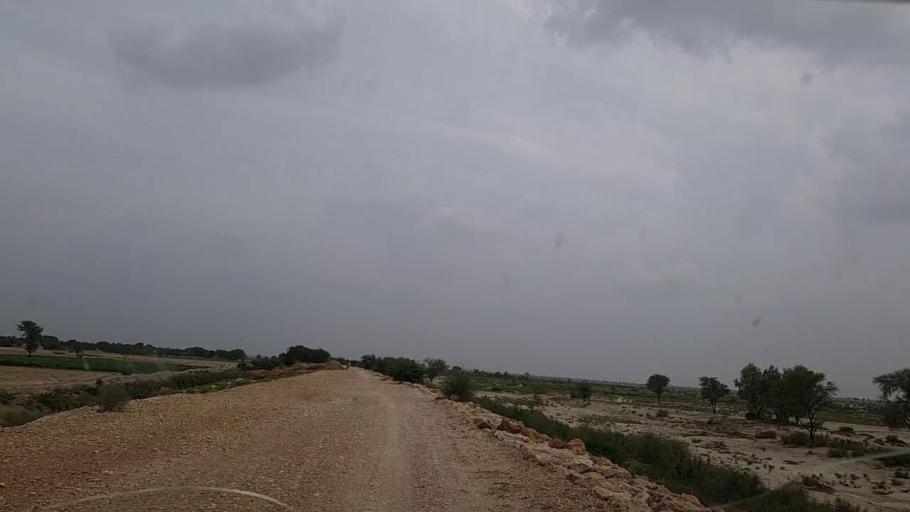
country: PK
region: Sindh
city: Johi
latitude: 26.7210
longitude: 67.5791
